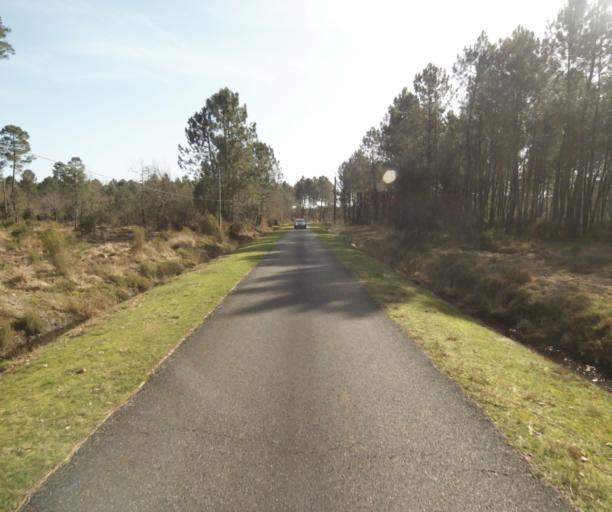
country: FR
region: Aquitaine
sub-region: Departement des Landes
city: Roquefort
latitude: 44.2164
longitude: -0.2435
